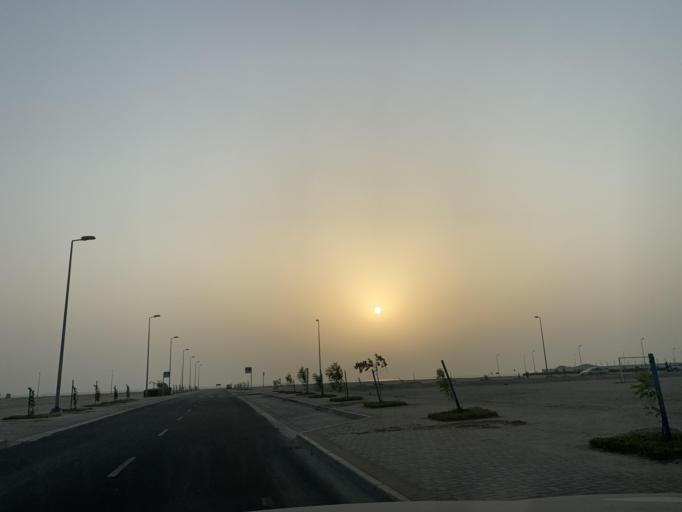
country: BH
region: Manama
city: Jidd Hafs
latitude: 26.2225
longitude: 50.4404
